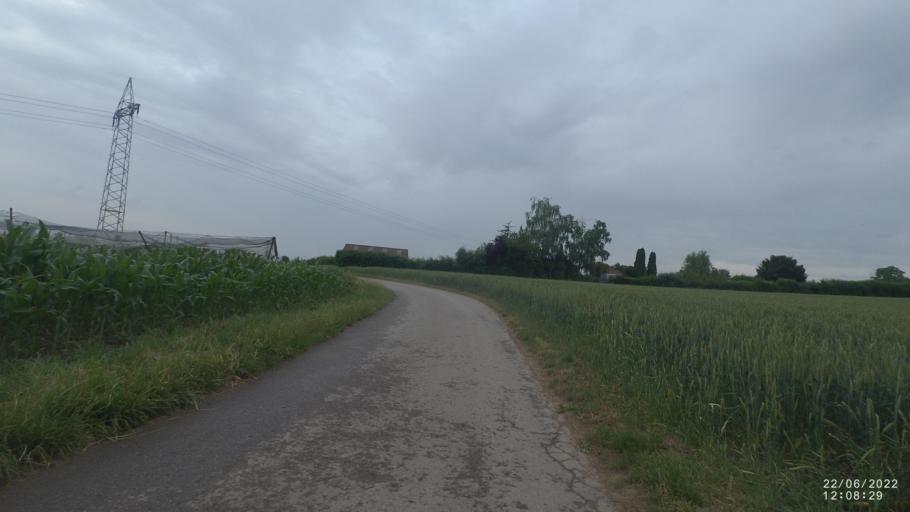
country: DE
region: Baden-Wuerttemberg
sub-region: Regierungsbezirk Stuttgart
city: Waiblingen
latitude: 48.8078
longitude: 9.3048
